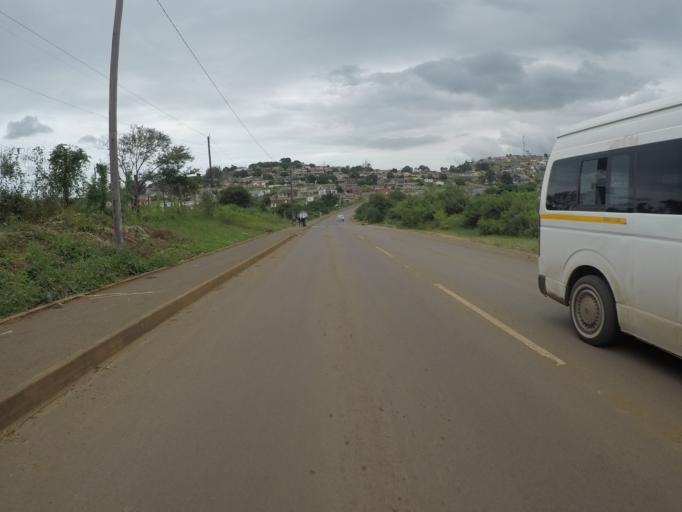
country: ZA
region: KwaZulu-Natal
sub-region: uThungulu District Municipality
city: Empangeni
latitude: -28.7805
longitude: 31.8632
